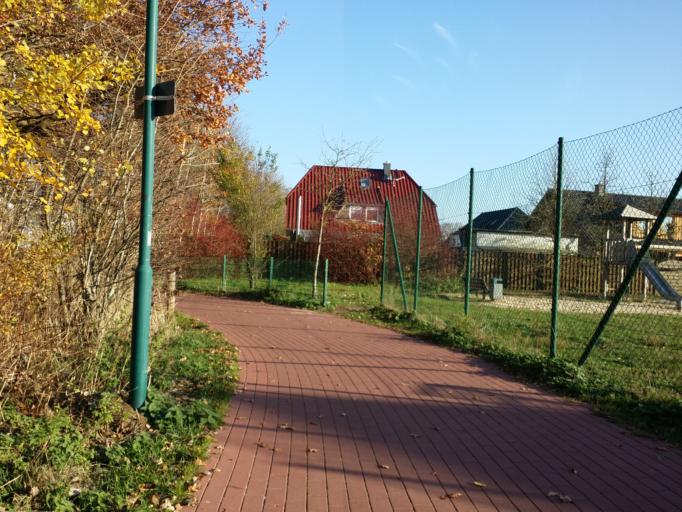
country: DE
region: Lower Saxony
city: Rotenburg
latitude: 53.0956
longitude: 9.3890
